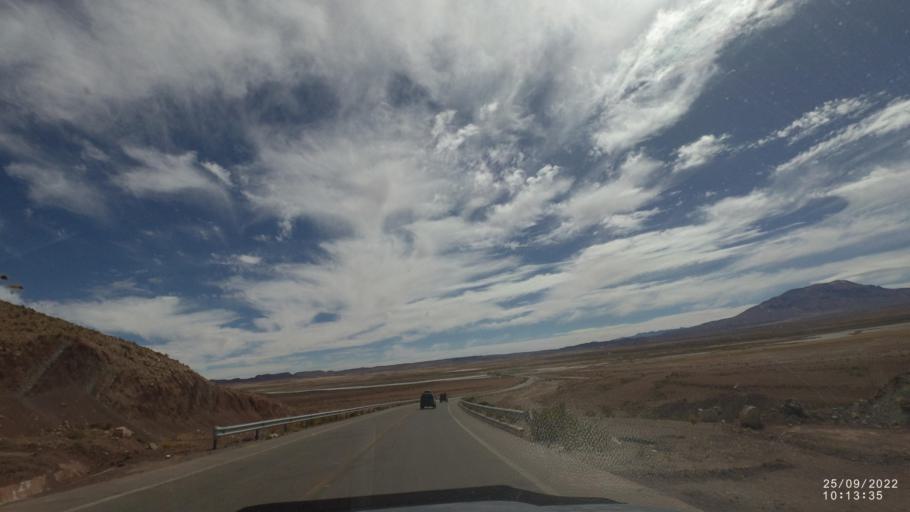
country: BO
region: Potosi
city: Colchani
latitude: -20.0718
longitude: -66.8870
